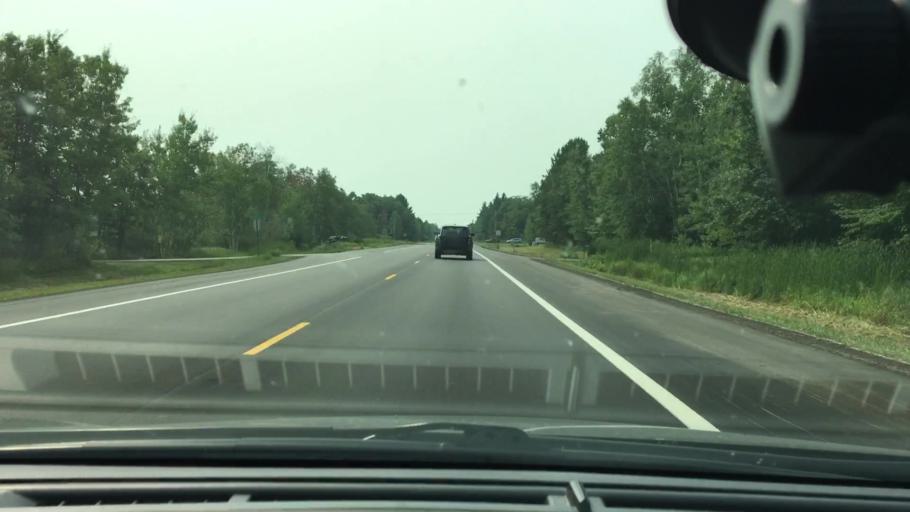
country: US
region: Minnesota
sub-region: Crow Wing County
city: Brainerd
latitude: 46.4524
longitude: -94.1722
